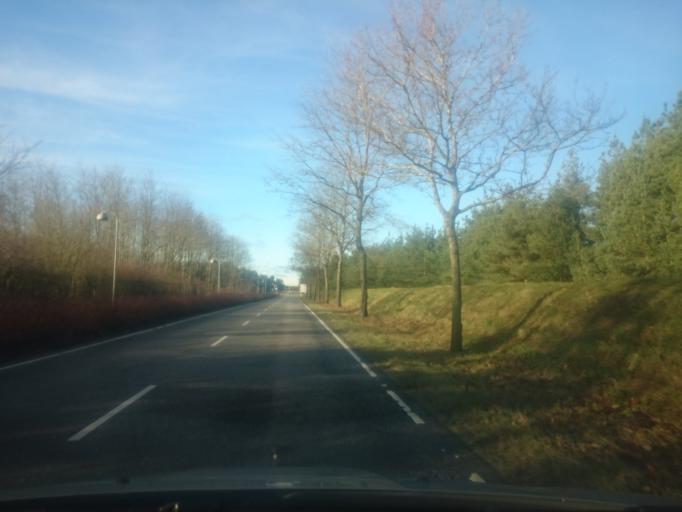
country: DK
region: South Denmark
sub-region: Billund Kommune
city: Billund
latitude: 55.7387
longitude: 9.1188
